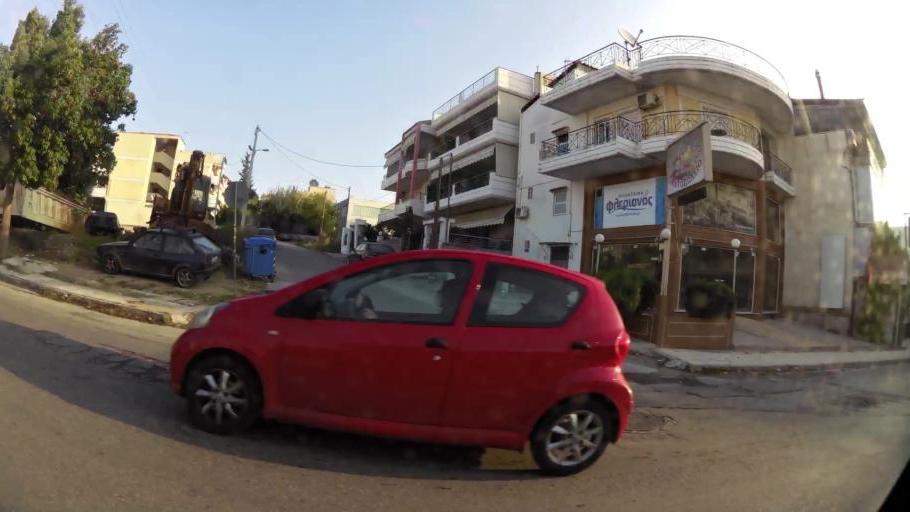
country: GR
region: Attica
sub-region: Nomarchia Dytikis Attikis
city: Zefyri
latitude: 38.0554
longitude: 23.7209
